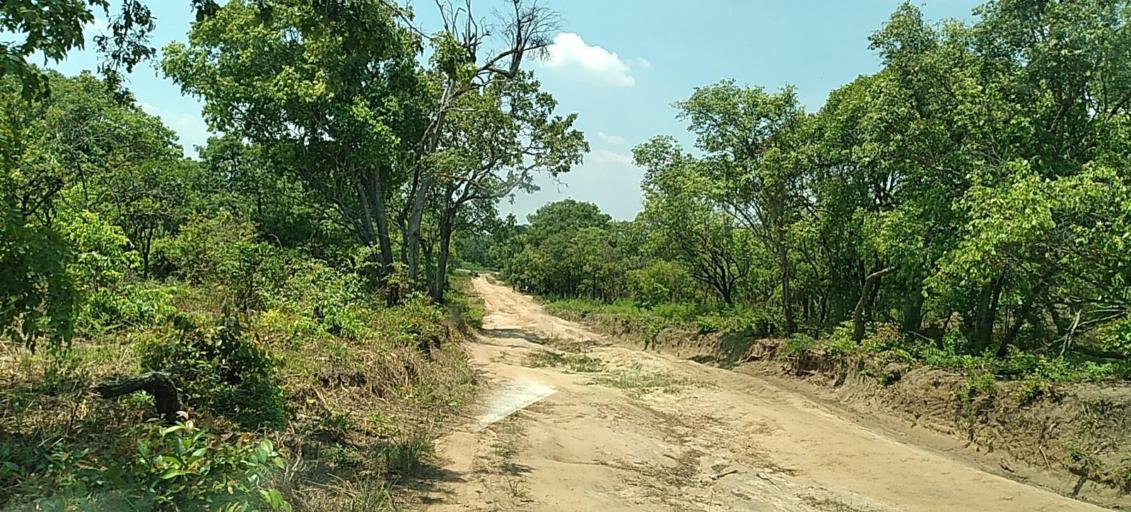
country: CD
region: Katanga
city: Kolwezi
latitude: -11.3152
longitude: 25.2347
